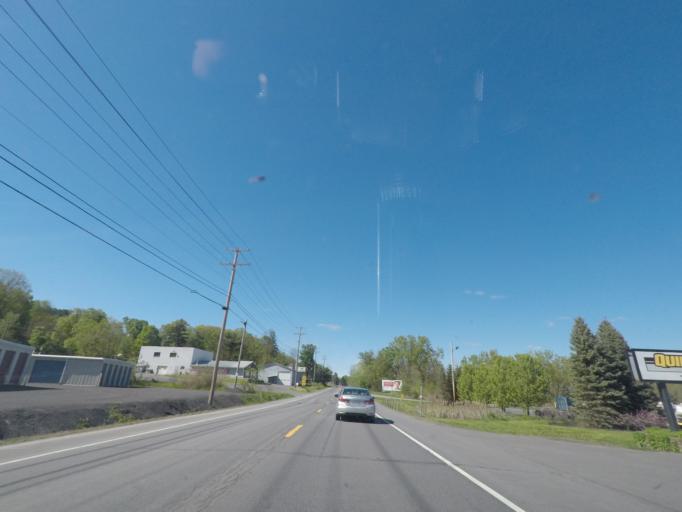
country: US
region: New York
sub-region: Albany County
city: Ravena
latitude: 42.4581
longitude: -73.8176
